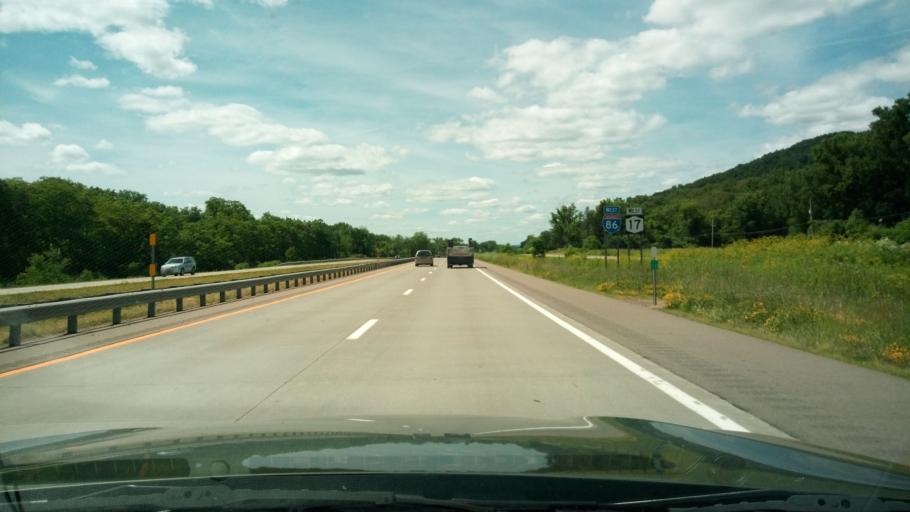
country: US
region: New York
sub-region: Chemung County
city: Southport
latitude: 42.0328
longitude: -76.7283
